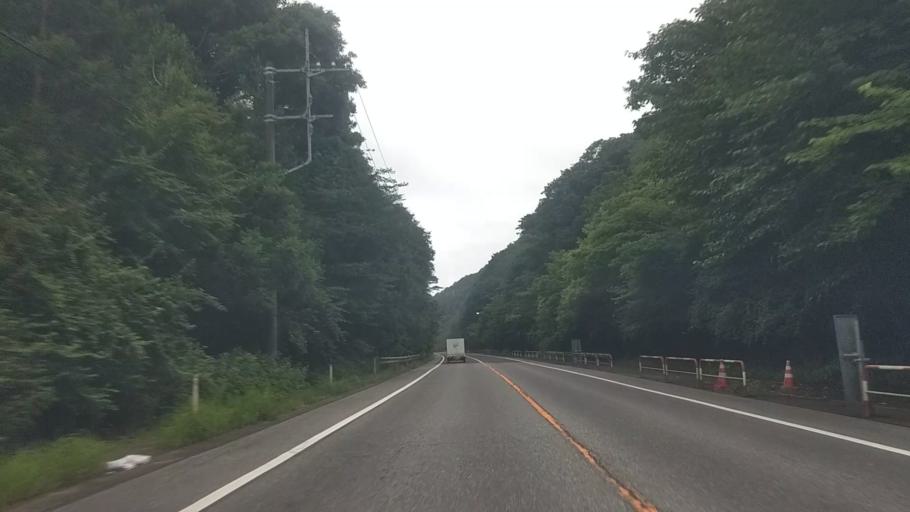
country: JP
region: Chiba
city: Kawaguchi
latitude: 35.1703
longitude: 140.0597
